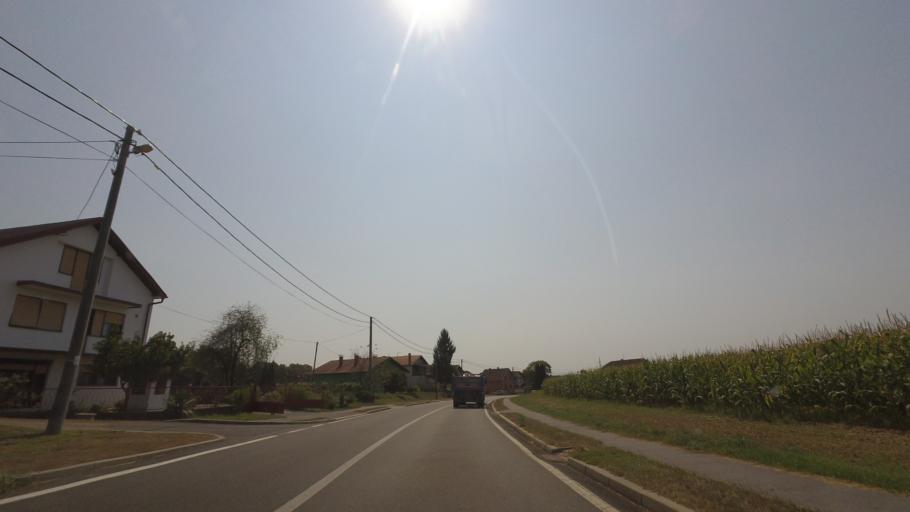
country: HR
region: Sisacko-Moslavacka
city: Novska
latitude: 45.3593
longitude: 16.9705
